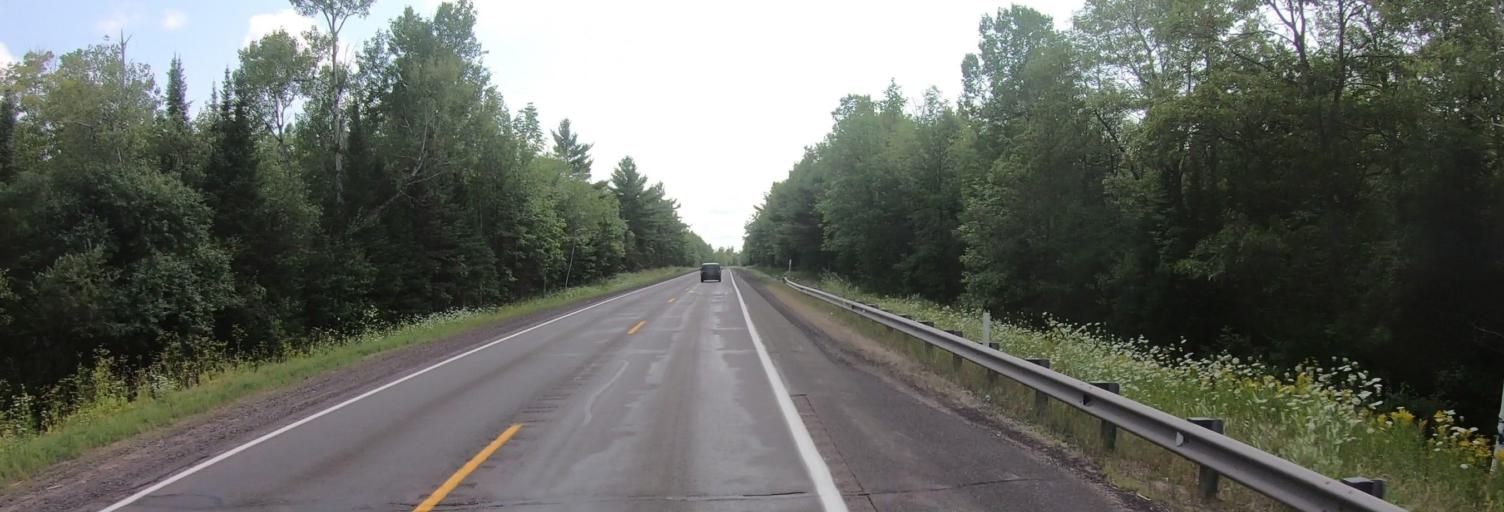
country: US
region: Michigan
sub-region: Ontonagon County
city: Ontonagon
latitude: 46.7408
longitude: -89.1080
